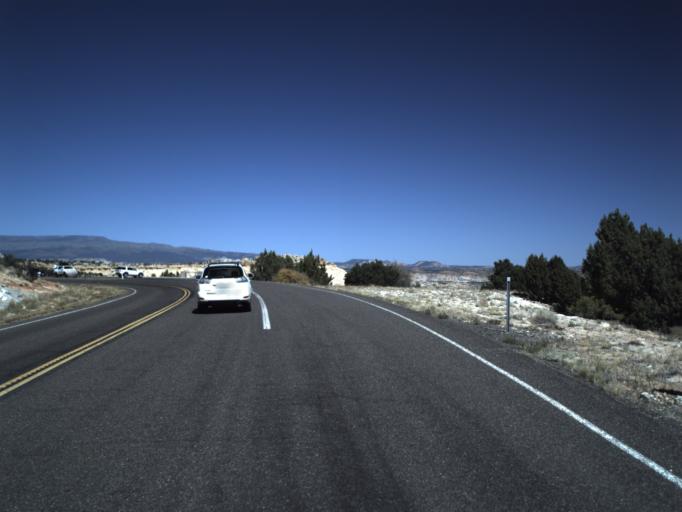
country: US
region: Utah
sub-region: Wayne County
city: Loa
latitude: 37.7454
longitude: -111.4545
